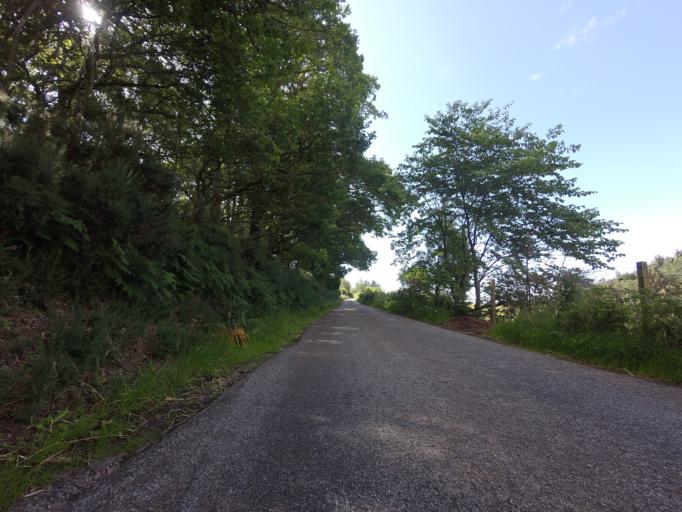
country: GB
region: Scotland
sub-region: Highland
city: Nairn
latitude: 57.5408
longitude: -3.8660
